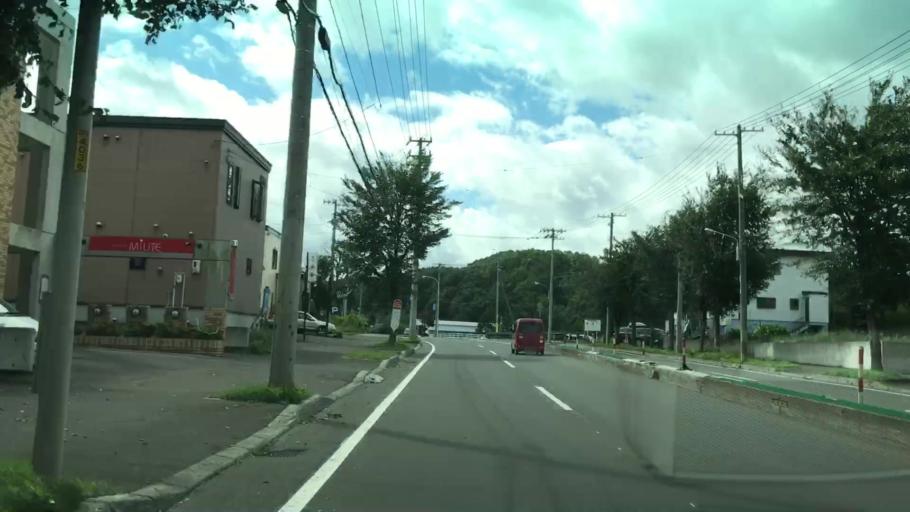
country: JP
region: Hokkaido
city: Sapporo
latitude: 42.9836
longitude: 141.4382
